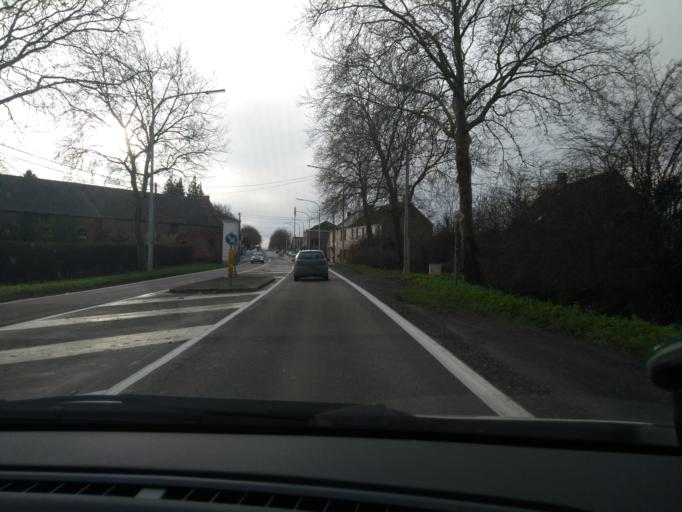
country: BE
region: Wallonia
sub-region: Province du Hainaut
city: Quevy-le-Petit
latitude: 50.3514
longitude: 3.9678
